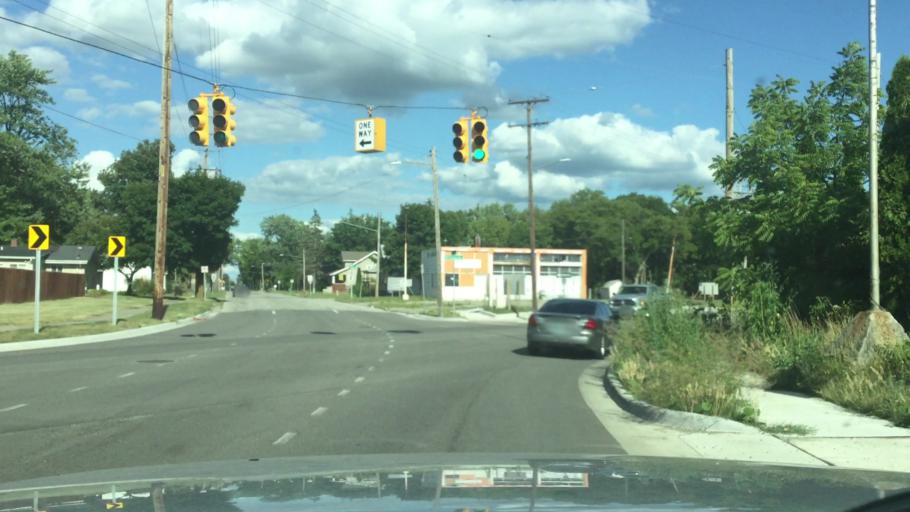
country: US
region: Michigan
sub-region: Saginaw County
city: Saginaw
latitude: 43.4004
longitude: -83.9506
